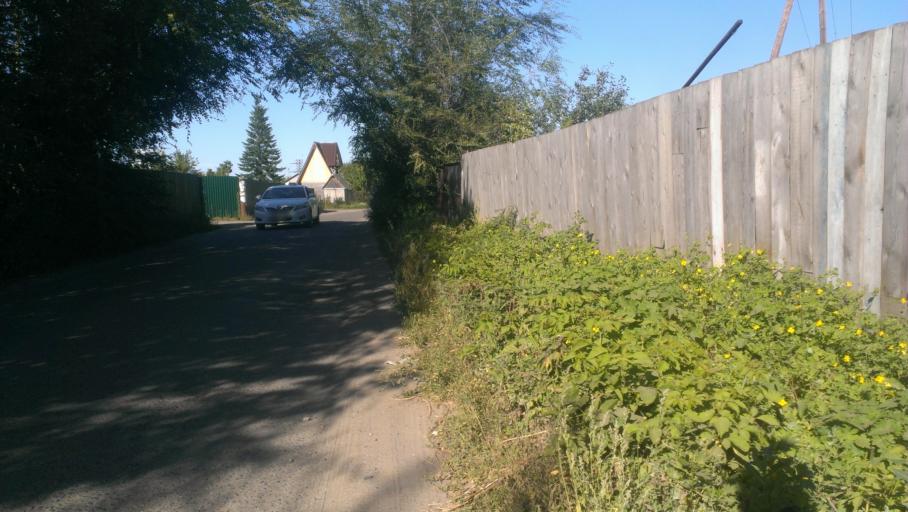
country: RU
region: Altai Krai
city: Novosilikatnyy
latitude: 53.3224
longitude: 83.6817
